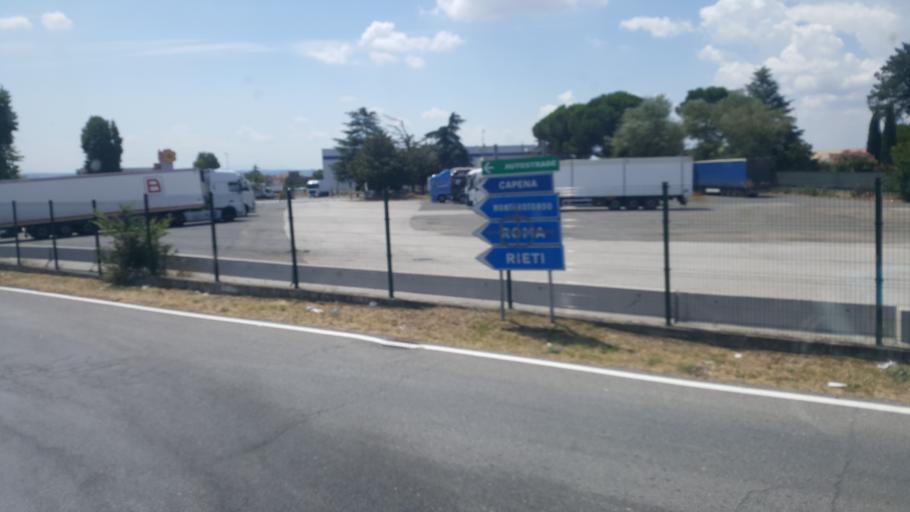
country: IT
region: Latium
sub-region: Citta metropolitana di Roma Capitale
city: Fiano Romano
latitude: 42.1401
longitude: 12.5959
